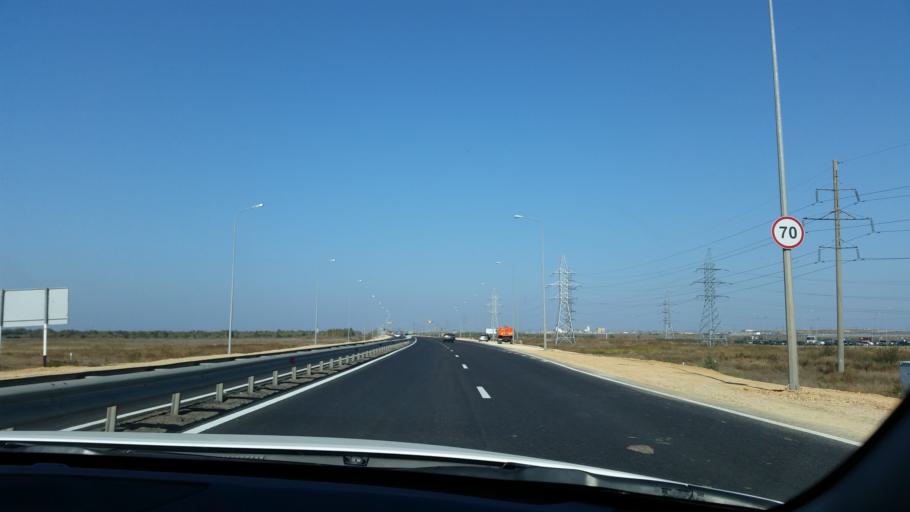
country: KZ
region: Astana Qalasy
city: Astana
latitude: 51.2069
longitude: 71.3126
